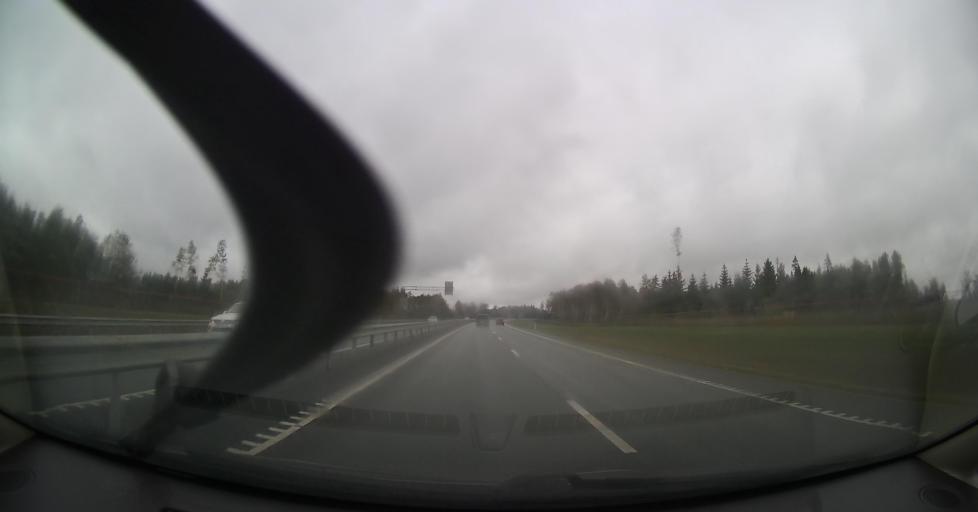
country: EE
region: Jaervamaa
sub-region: Paide linn
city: Paide
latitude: 59.0355
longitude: 25.4471
